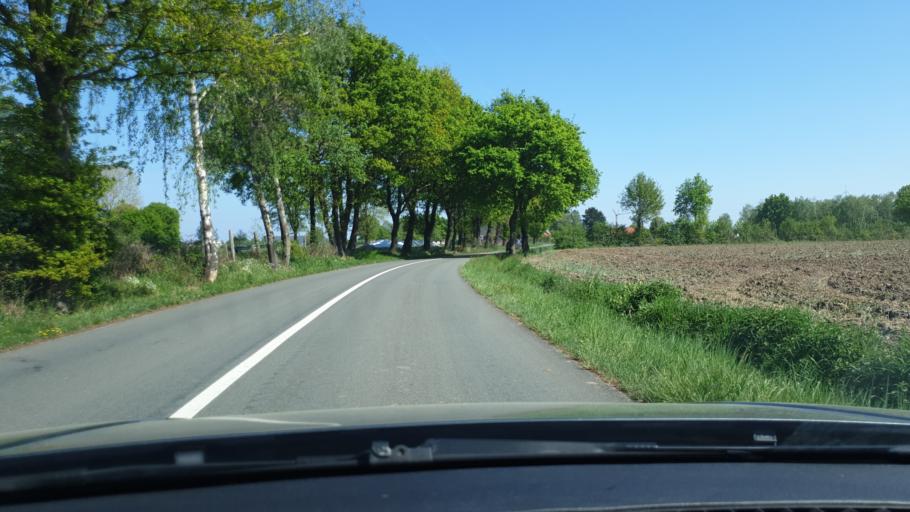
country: BE
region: Flanders
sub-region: Provincie Antwerpen
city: Geel
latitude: 51.1564
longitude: 4.9468
